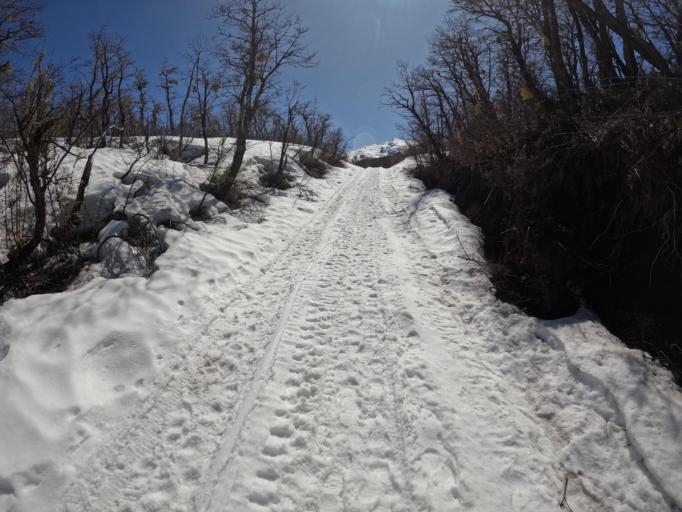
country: CL
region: Araucania
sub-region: Provincia de Cautin
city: Vilcun
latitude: -38.6603
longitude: -71.6187
